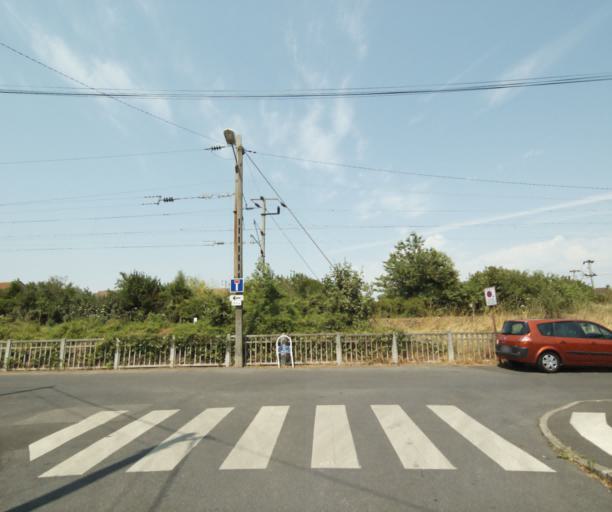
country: FR
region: Ile-de-France
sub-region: Departement des Yvelines
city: Conflans-Sainte-Honorine
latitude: 48.9949
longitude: 2.0923
